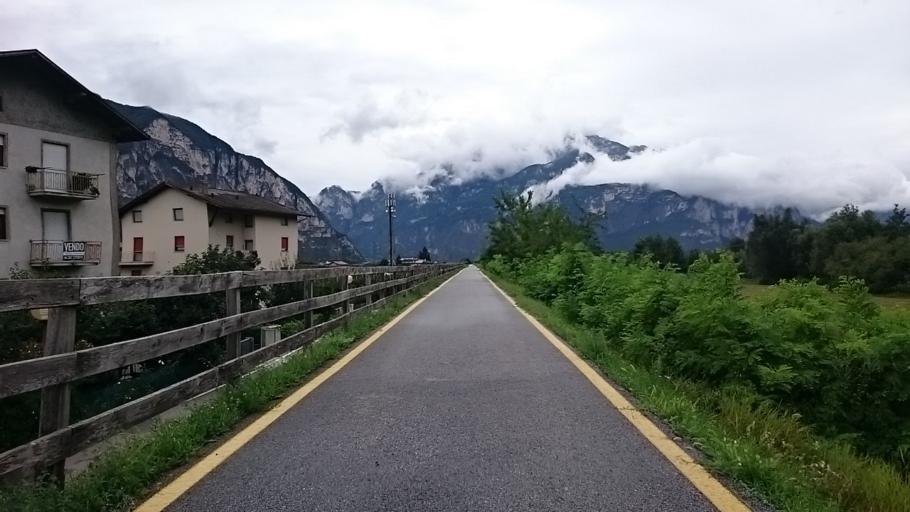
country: IT
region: Trentino-Alto Adige
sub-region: Provincia di Trento
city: Nave San Rocco
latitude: 46.1695
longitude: 11.1111
